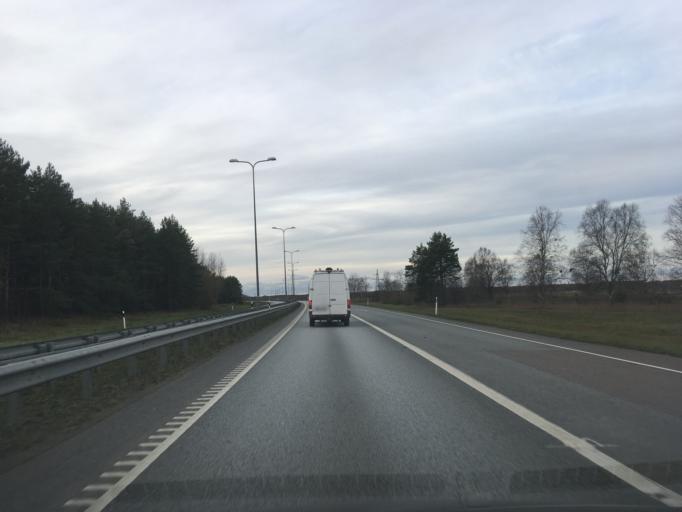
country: EE
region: Ida-Virumaa
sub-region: Kohtla-Jaerve linn
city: Kohtla-Jarve
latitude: 59.4054
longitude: 27.3241
